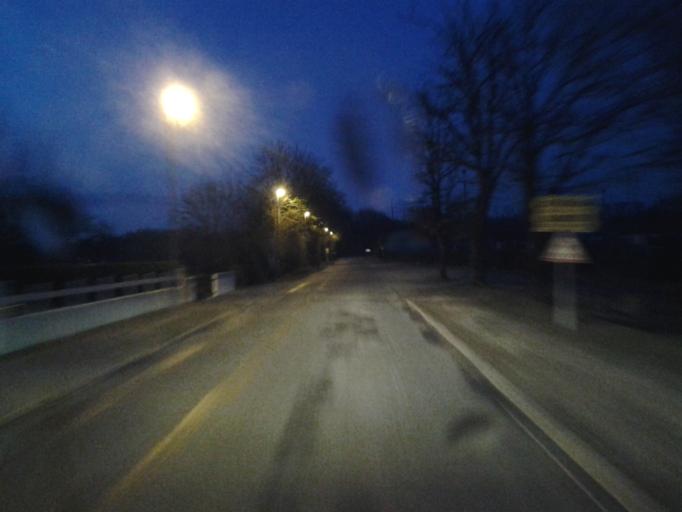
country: FR
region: Pays de la Loire
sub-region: Departement de la Vendee
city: Saint-Florent-des-Bois
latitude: 46.5904
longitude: -1.3149
